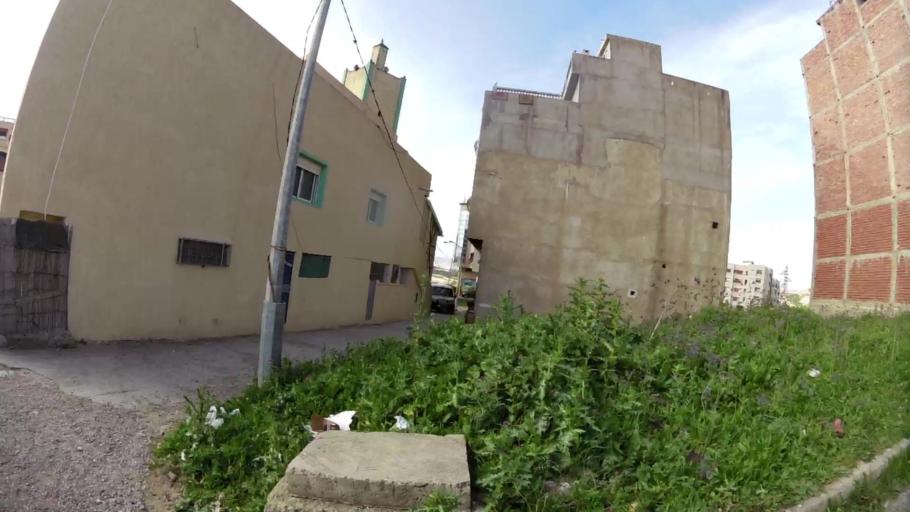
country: MA
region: Tanger-Tetouan
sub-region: Tanger-Assilah
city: Tangier
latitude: 35.7660
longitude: -5.7731
